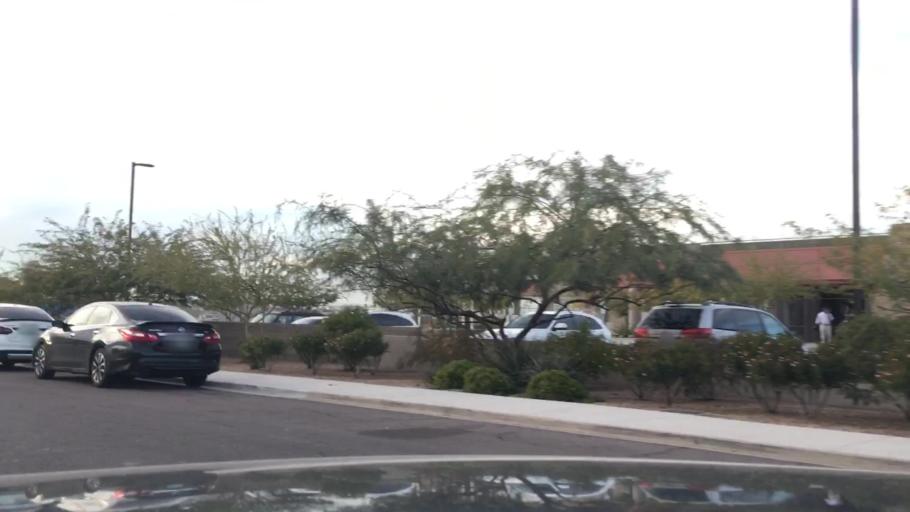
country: US
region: Arizona
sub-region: Maricopa County
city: Mesa
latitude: 33.4774
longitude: -111.7313
